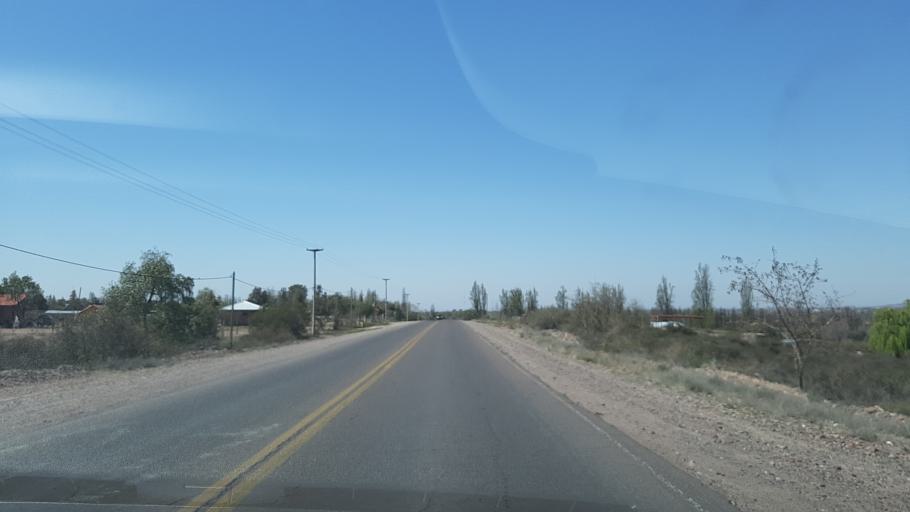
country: AR
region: Mendoza
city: Lujan de Cuyo
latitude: -33.0183
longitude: -68.9425
